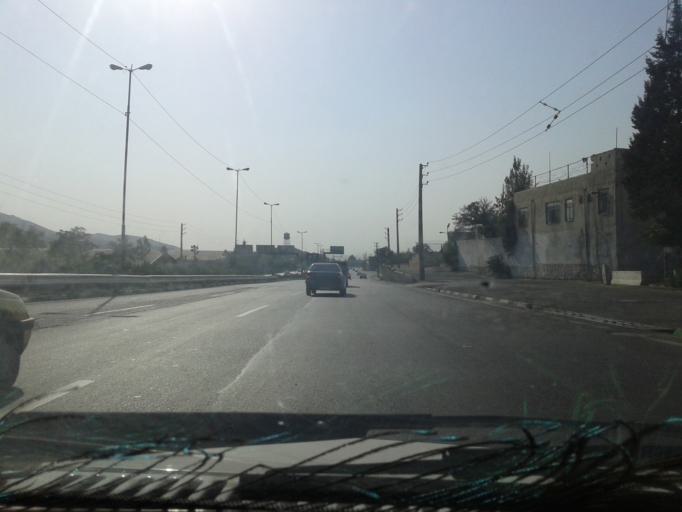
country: IR
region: Tehran
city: Tehran
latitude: 35.7239
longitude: 51.5802
